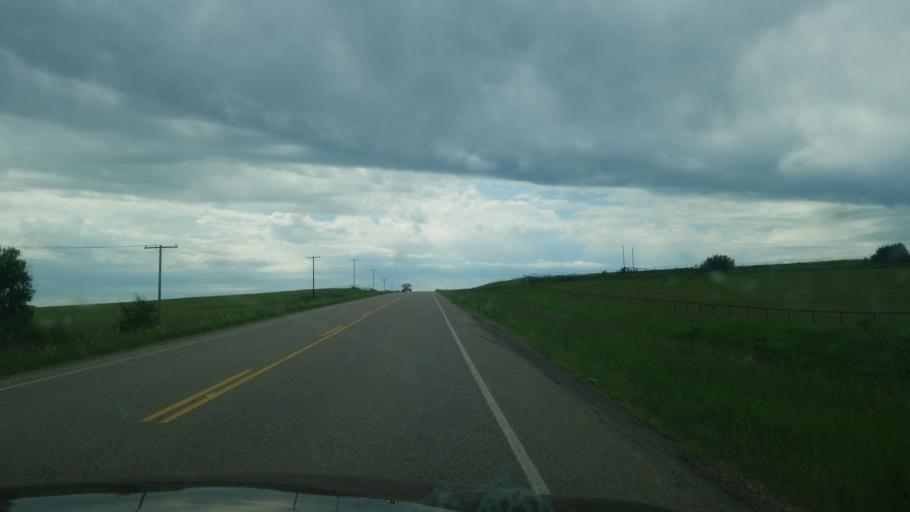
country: CA
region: Saskatchewan
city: Unity
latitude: 52.9728
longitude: -109.3426
